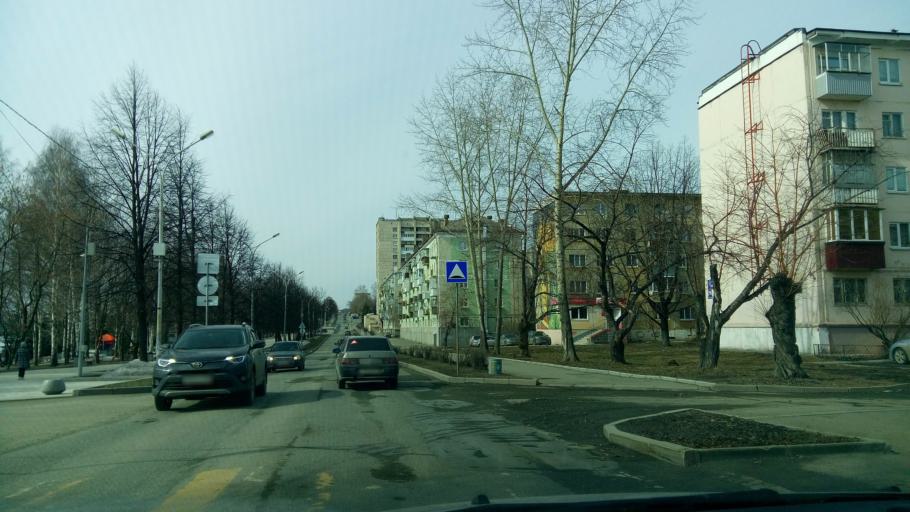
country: RU
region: Sverdlovsk
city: Nizhniy Tagil
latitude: 57.9056
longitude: 59.9787
